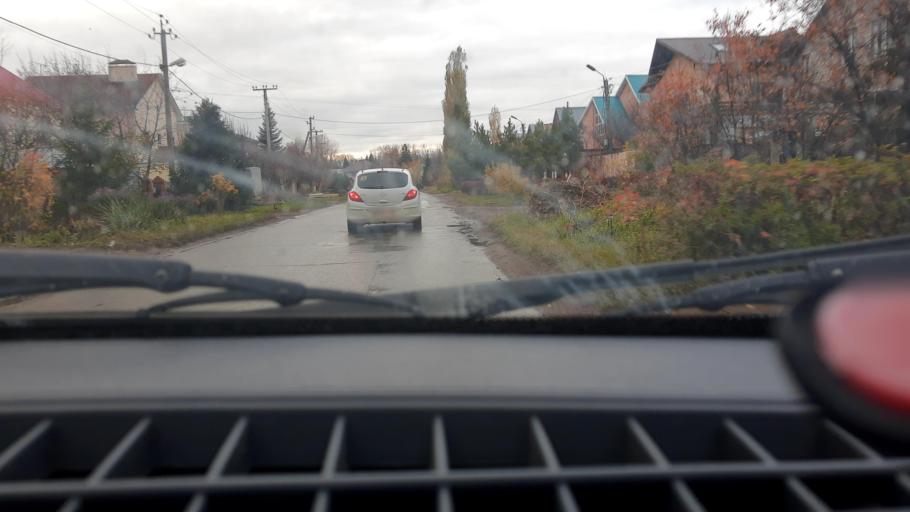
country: RU
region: Bashkortostan
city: Mikhaylovka
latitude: 54.7934
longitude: 55.9433
